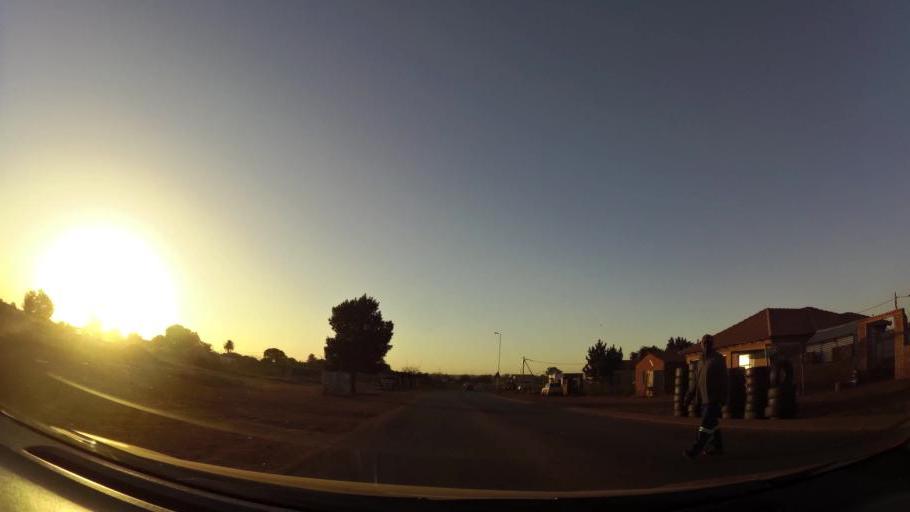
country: ZA
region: Gauteng
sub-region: City of Tshwane Metropolitan Municipality
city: Mabopane
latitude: -25.5901
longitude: 28.0903
